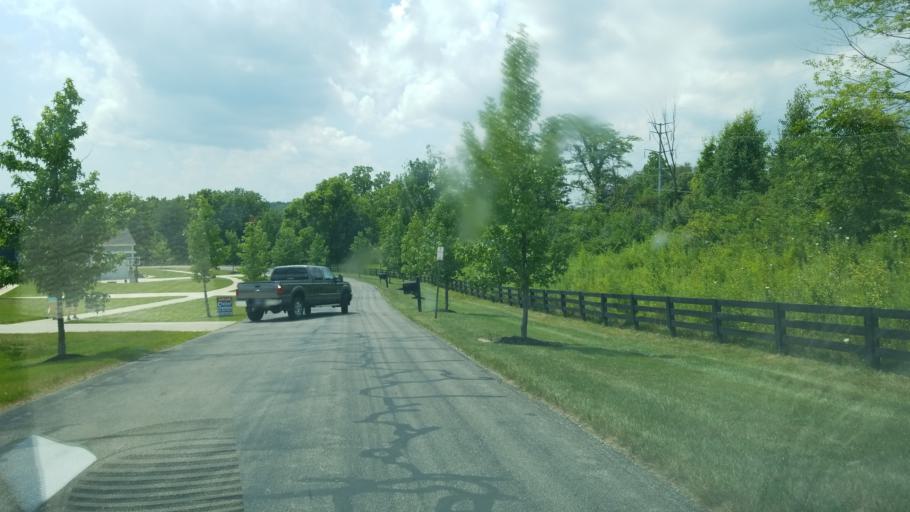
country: US
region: Ohio
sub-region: Delaware County
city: Lewis Center
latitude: 40.2143
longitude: -83.0548
